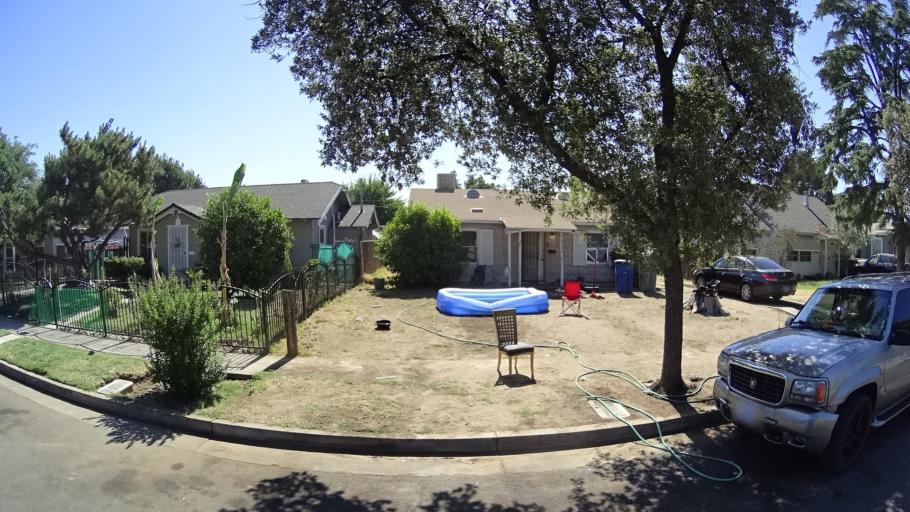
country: US
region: California
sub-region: Fresno County
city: Fresno
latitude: 36.7639
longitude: -119.8188
